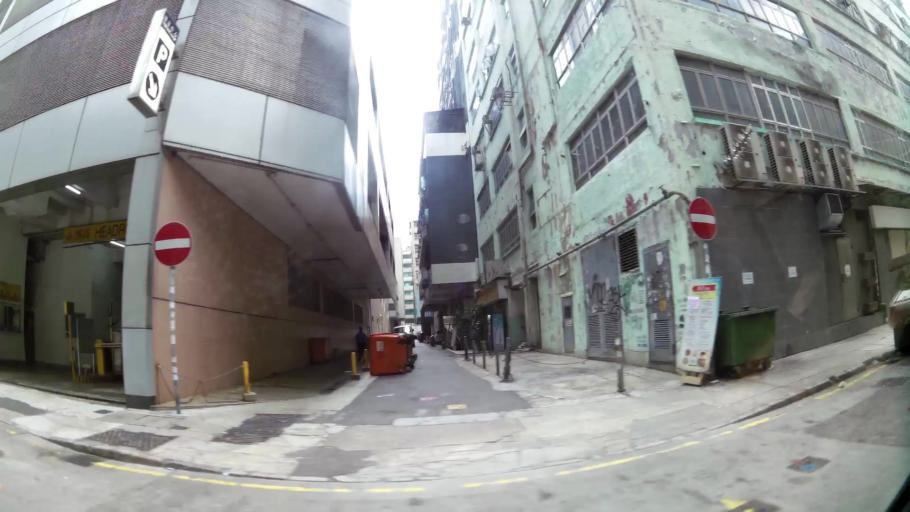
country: HK
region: Kowloon City
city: Kowloon
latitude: 22.3141
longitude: 114.2192
